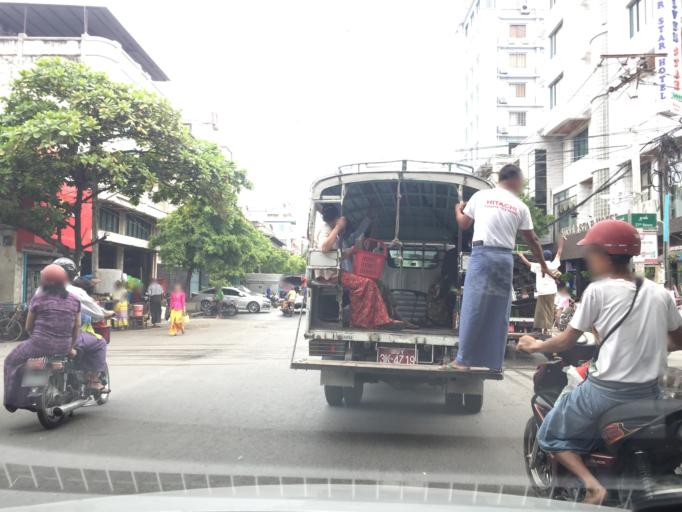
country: MM
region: Mandalay
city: Mandalay
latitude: 21.9818
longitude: 96.0794
